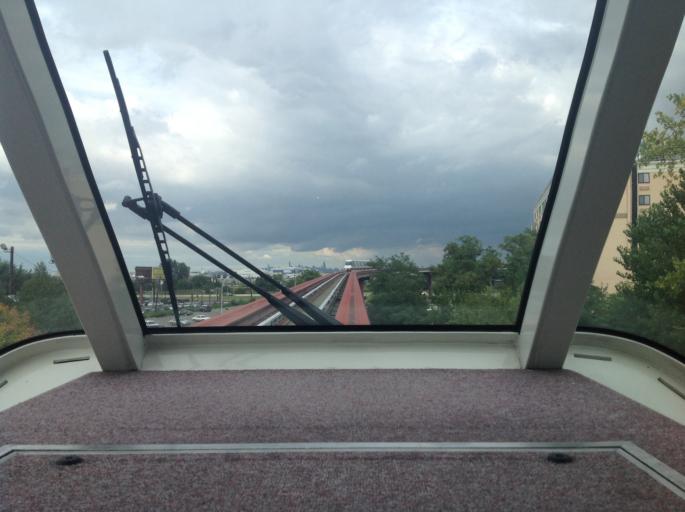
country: US
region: New Jersey
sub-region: Essex County
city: Newark
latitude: 40.6994
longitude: -74.1862
